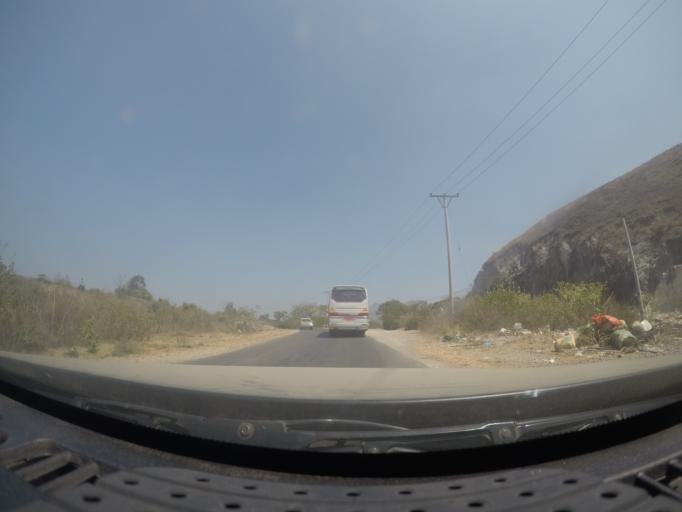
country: MM
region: Shan
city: Taunggyi
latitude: 20.9432
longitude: 96.5477
